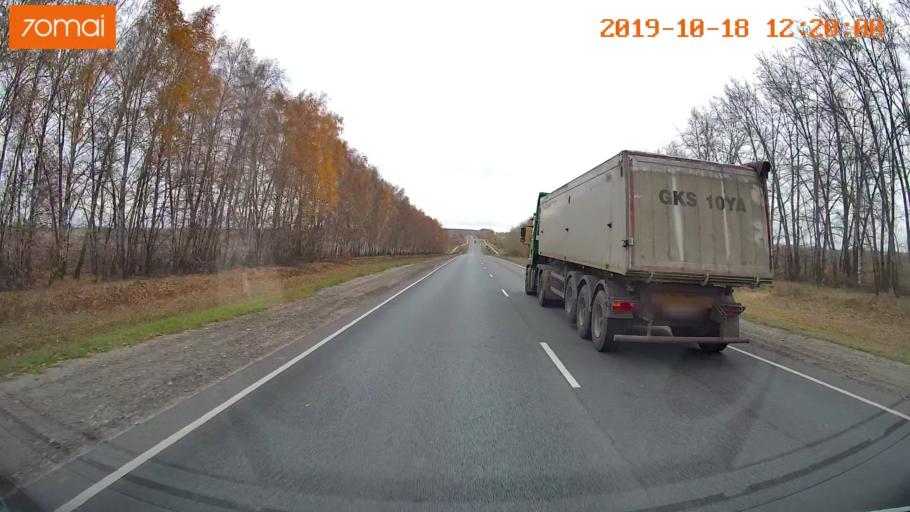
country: RU
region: Rjazan
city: Zakharovo
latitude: 54.4908
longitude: 39.4747
